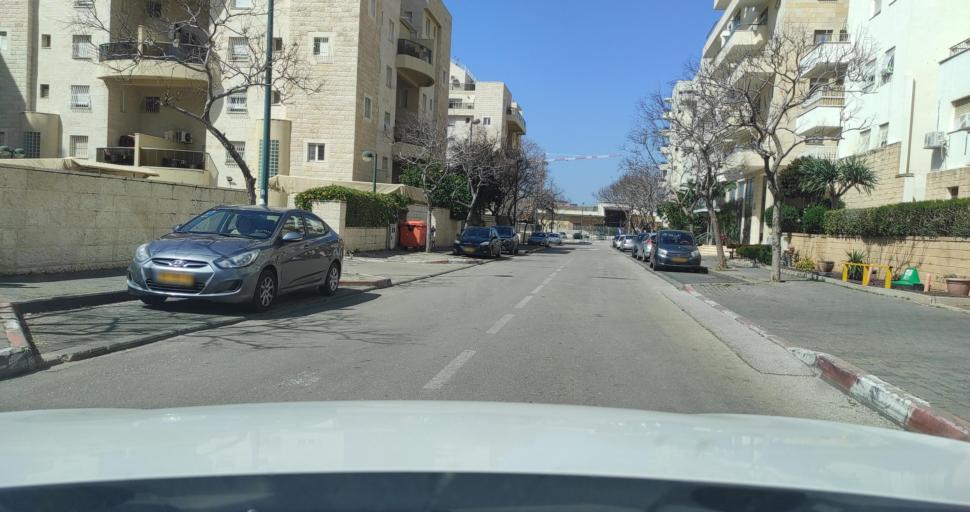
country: IL
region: Central District
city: Bet Yizhaq
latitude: 32.3091
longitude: 34.8715
